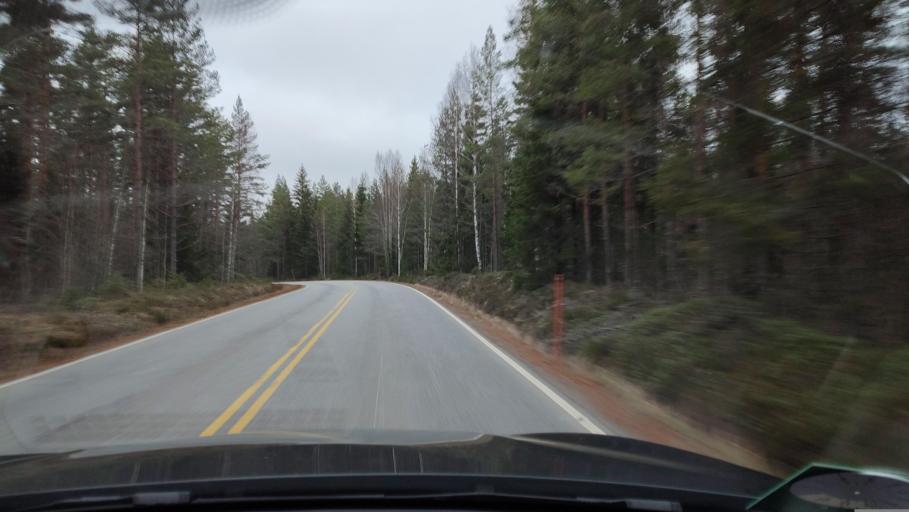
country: FI
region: Southern Ostrobothnia
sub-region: Suupohja
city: Karijoki
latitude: 62.2545
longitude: 21.7482
